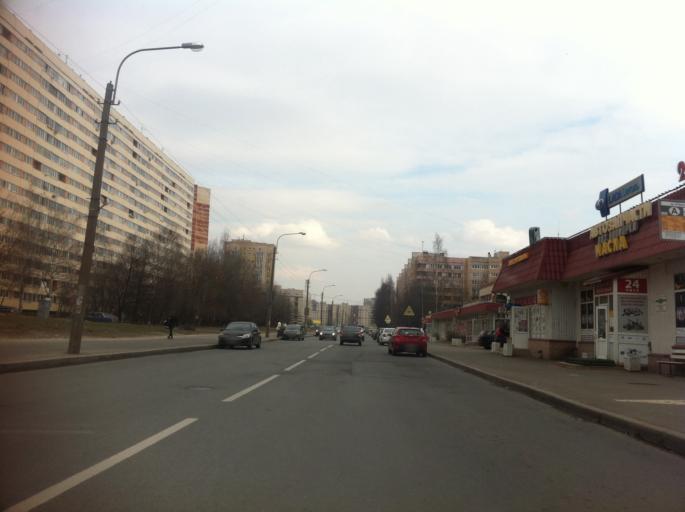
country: RU
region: St.-Petersburg
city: Uritsk
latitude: 59.8505
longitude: 30.1856
